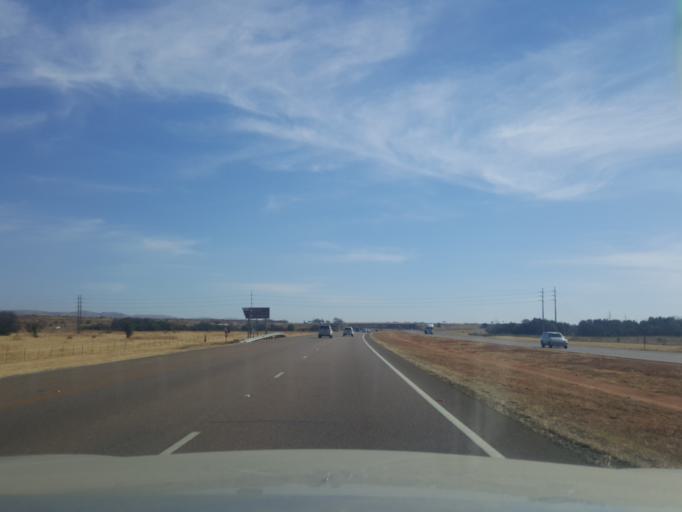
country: ZA
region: Gauteng
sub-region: City of Tshwane Metropolitan Municipality
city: Pretoria
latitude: -25.6463
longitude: 28.1608
